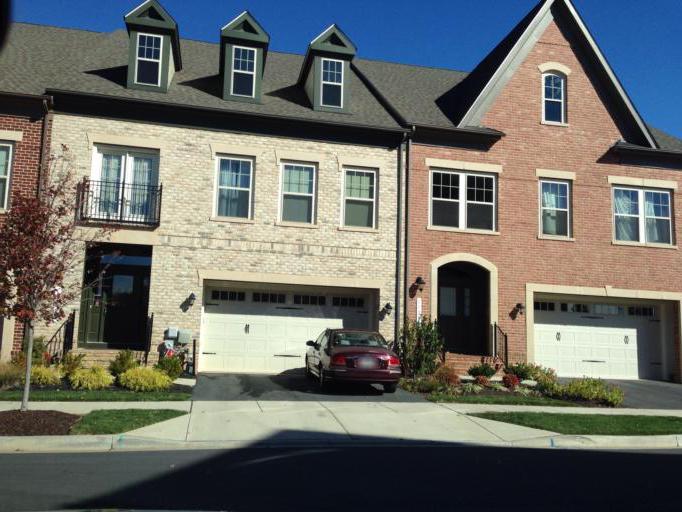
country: US
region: Maryland
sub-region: Howard County
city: Fulton
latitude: 39.1530
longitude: -76.9055
